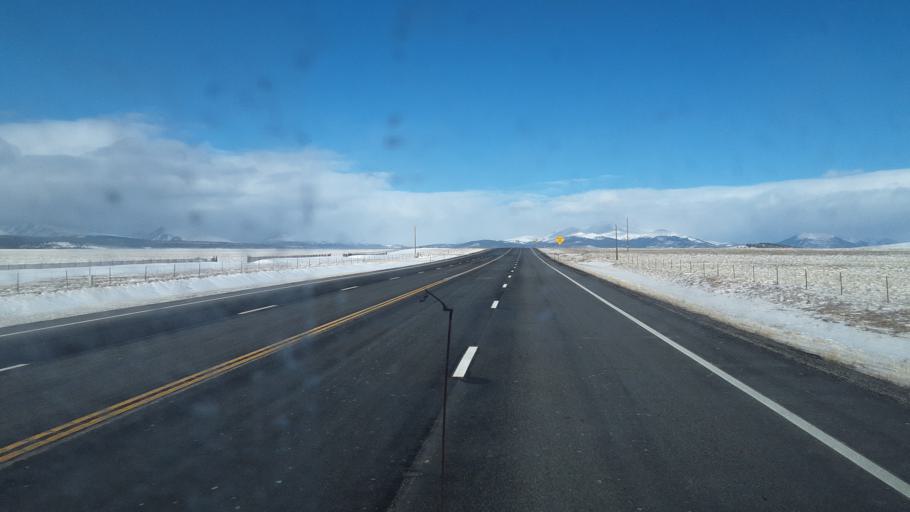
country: US
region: Colorado
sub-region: Park County
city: Fairplay
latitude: 39.1413
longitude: -105.9975
